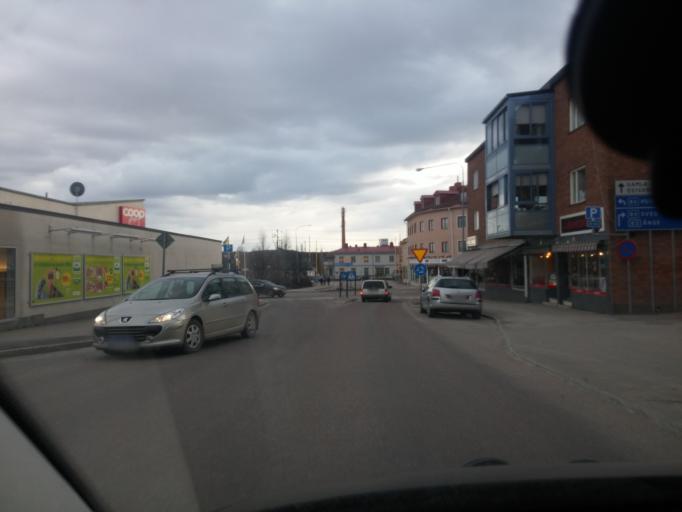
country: SE
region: Gaevleborg
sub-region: Ljusdals Kommun
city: Ljusdal
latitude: 61.8293
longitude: 16.0920
